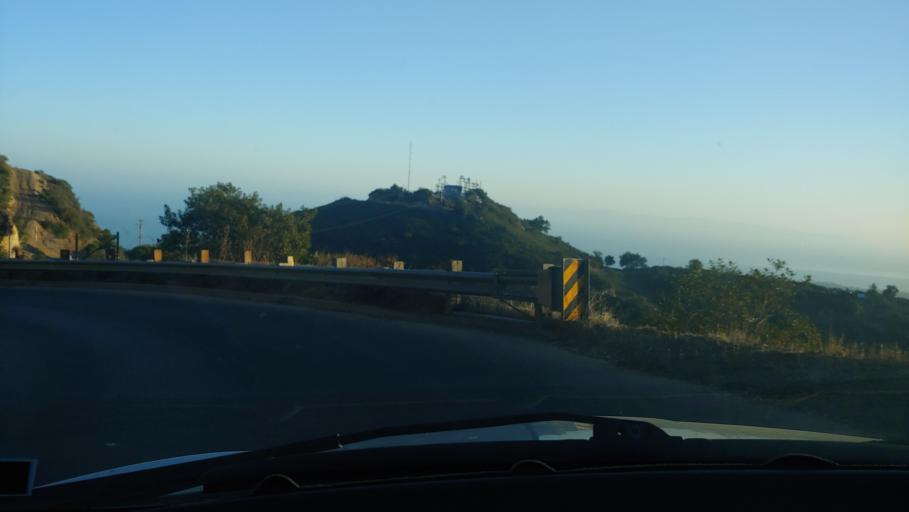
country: US
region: California
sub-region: Santa Barbara County
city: Mission Canyon
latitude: 34.4699
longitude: -119.6780
